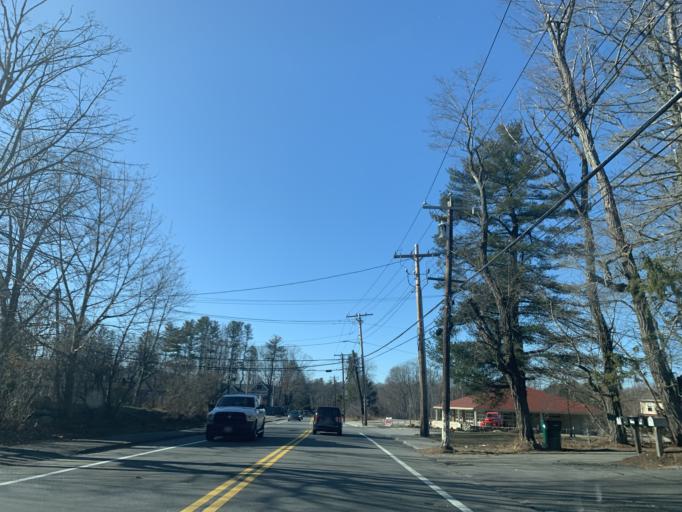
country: US
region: Massachusetts
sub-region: Middlesex County
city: Wayland
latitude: 42.3603
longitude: -71.3429
